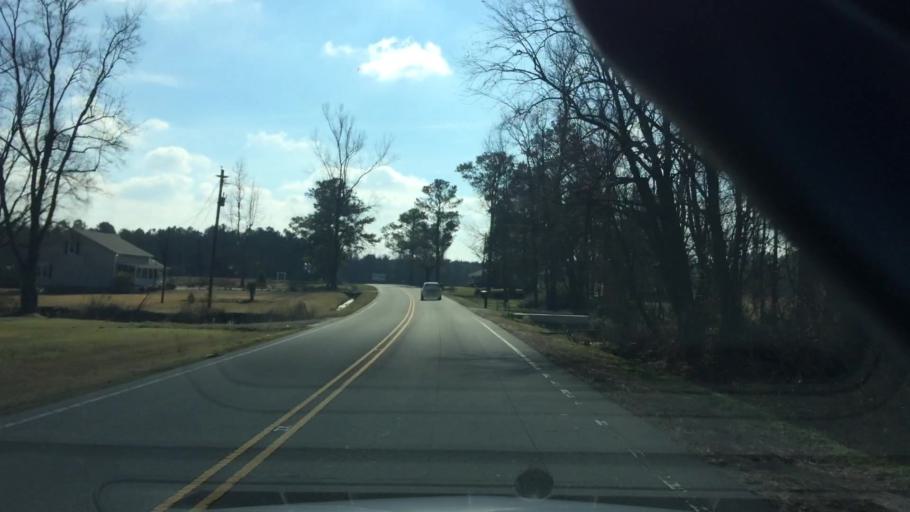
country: US
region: North Carolina
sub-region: Duplin County
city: Beulaville
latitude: 34.8557
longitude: -77.7978
